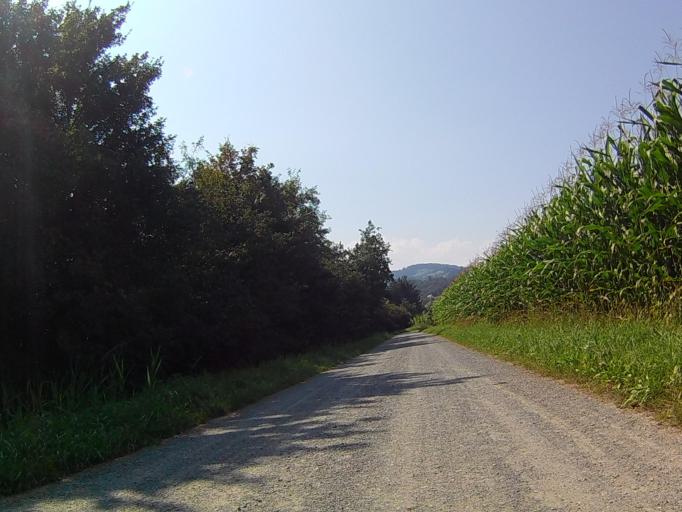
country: AT
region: Styria
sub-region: Politischer Bezirk Leibnitz
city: Oberhaag
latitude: 46.6872
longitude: 15.3424
